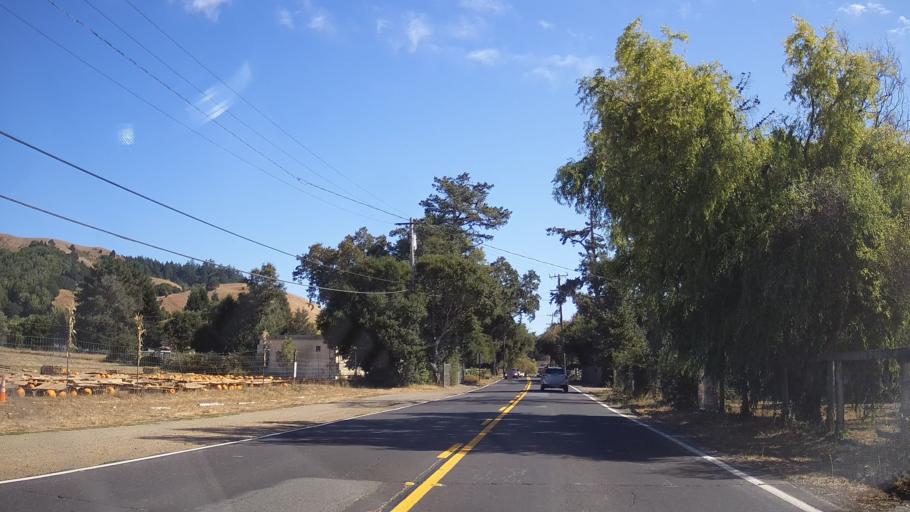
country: US
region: California
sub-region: Marin County
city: Lagunitas-Forest Knolls
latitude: 38.0638
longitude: -122.7007
